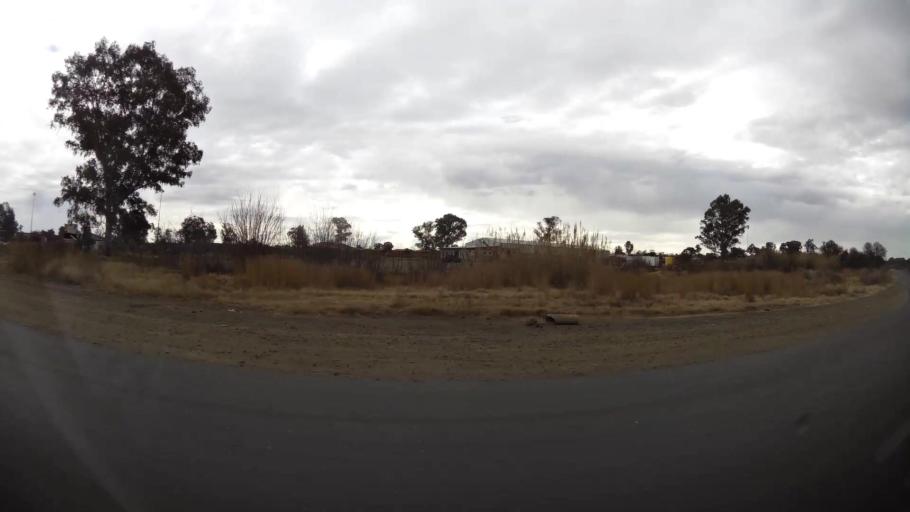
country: ZA
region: Orange Free State
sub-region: Fezile Dabi District Municipality
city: Kroonstad
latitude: -27.6554
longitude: 27.2262
